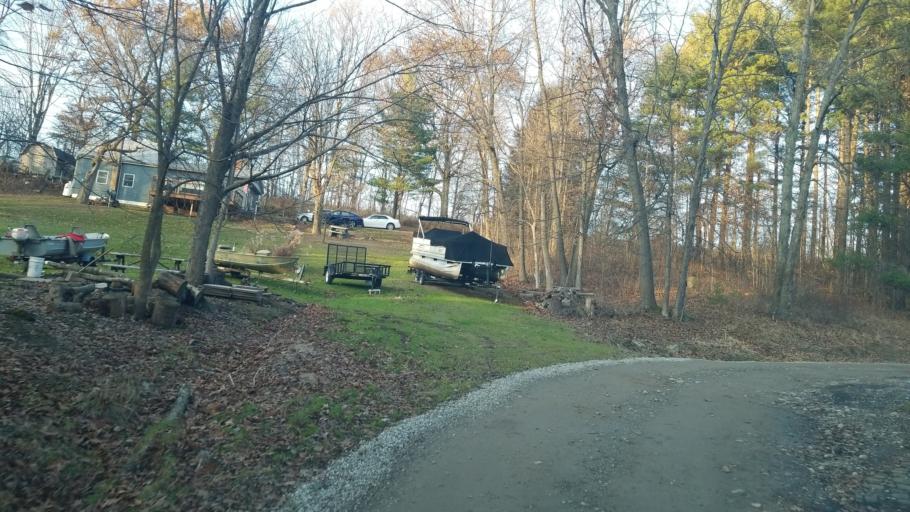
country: US
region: Ohio
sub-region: Sandusky County
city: Bellville
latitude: 40.5935
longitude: -82.5557
